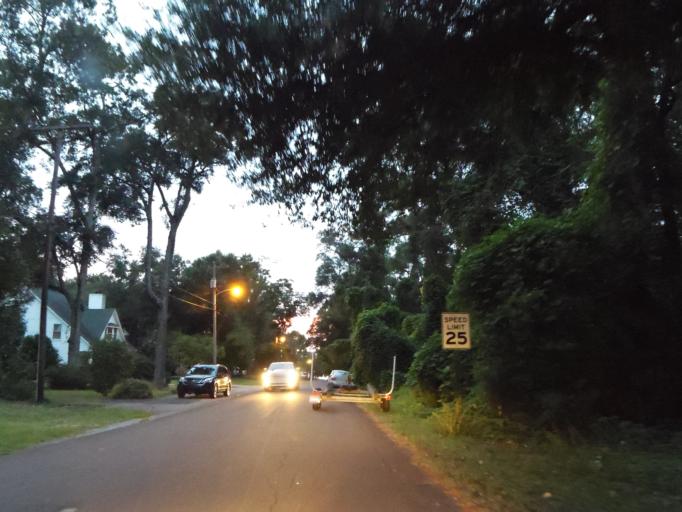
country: US
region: Alabama
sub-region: Baldwin County
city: Fairhope
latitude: 30.5401
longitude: -87.8999
